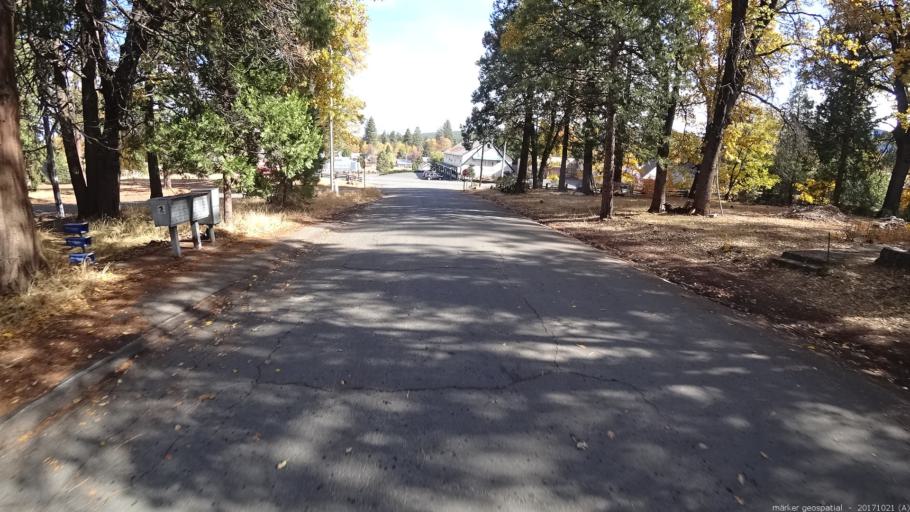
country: US
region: California
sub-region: Shasta County
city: Burney
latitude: 40.8814
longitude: -121.6732
